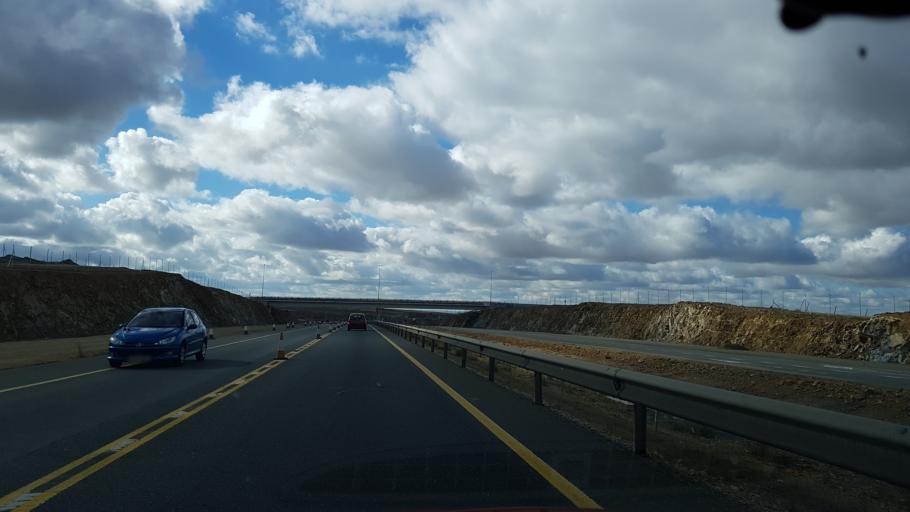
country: ES
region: Castille and Leon
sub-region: Provincia de Segovia
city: Segovia
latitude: 40.9214
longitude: -4.0991
